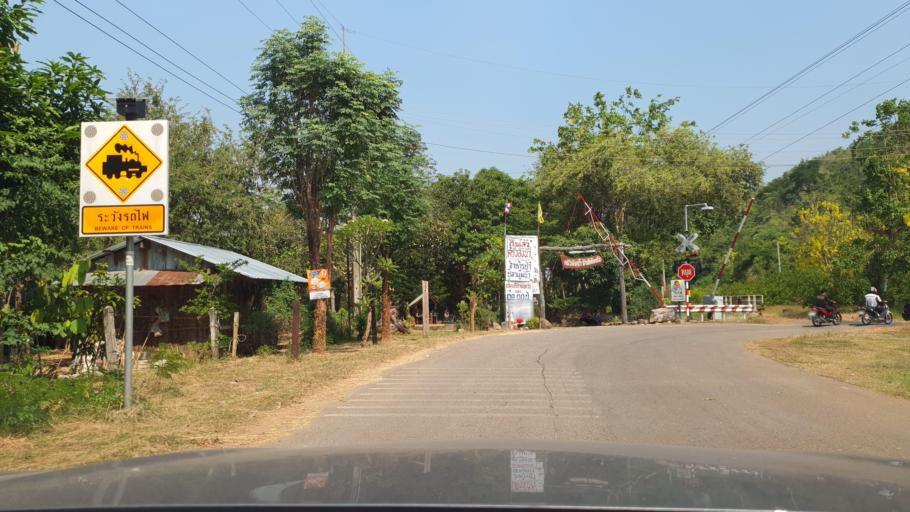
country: TH
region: Kanchanaburi
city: Sai Yok
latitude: 14.0957
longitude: 99.1754
